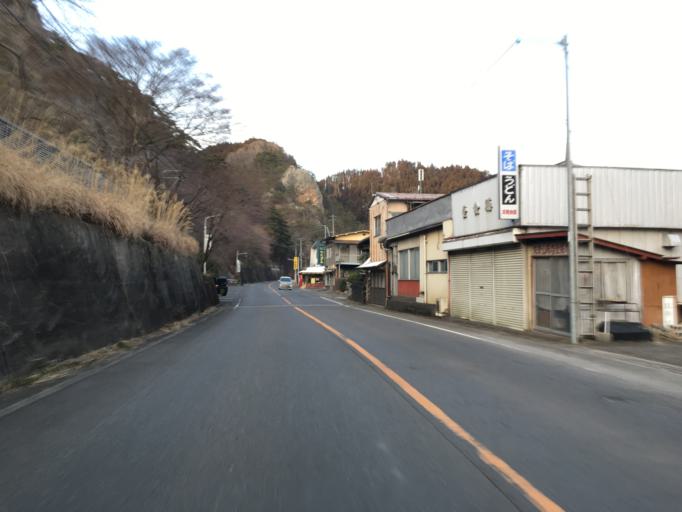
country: JP
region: Ibaraki
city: Daigo
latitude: 36.8514
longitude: 140.3969
